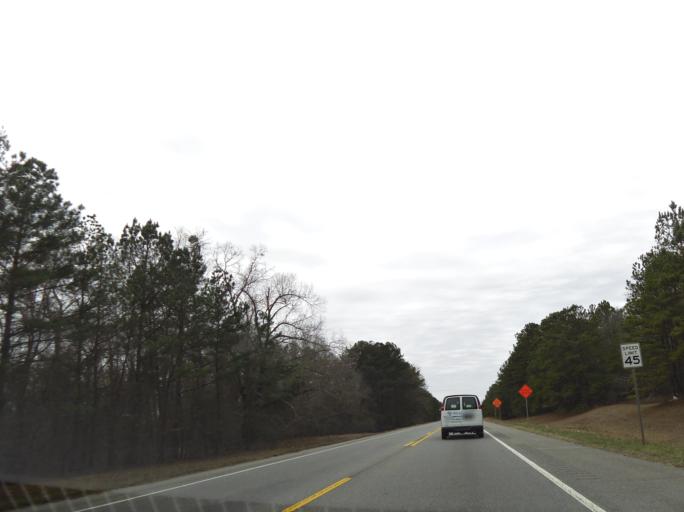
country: US
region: Georgia
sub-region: Bibb County
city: West Point
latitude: 32.7992
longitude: -83.7886
